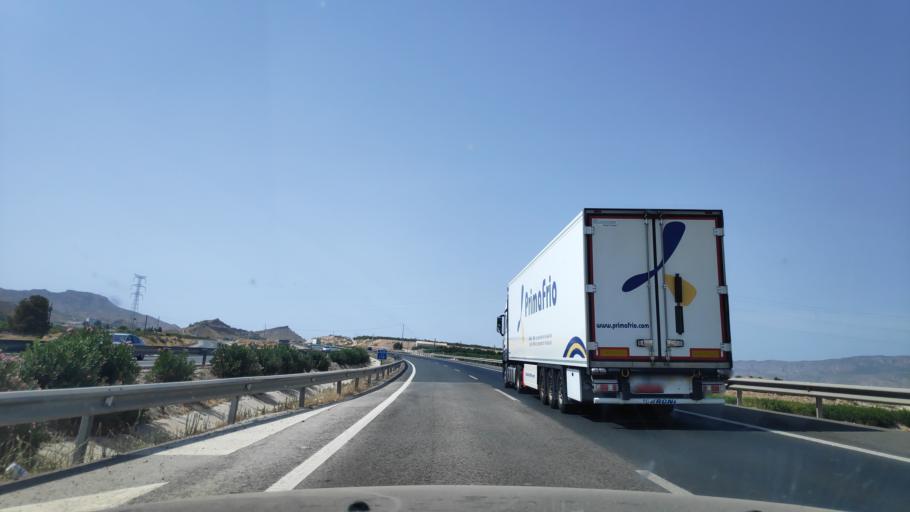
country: ES
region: Murcia
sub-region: Murcia
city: Archena
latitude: 38.1442
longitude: -1.2745
